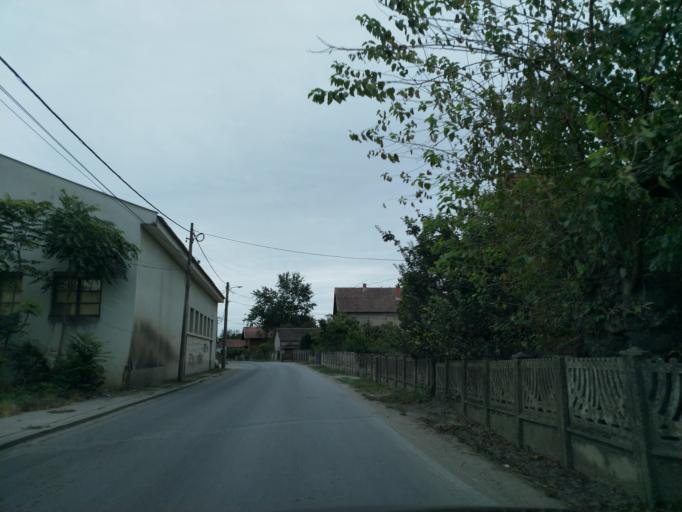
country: RS
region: Central Serbia
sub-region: Pomoravski Okrug
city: Paracin
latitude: 43.8263
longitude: 21.3544
